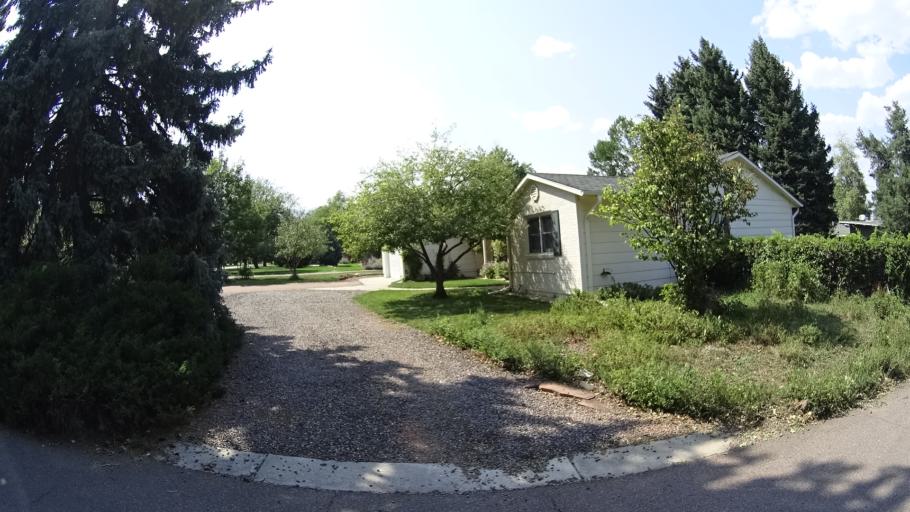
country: US
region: Colorado
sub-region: El Paso County
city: Colorado Springs
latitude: 38.7997
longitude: -104.8320
